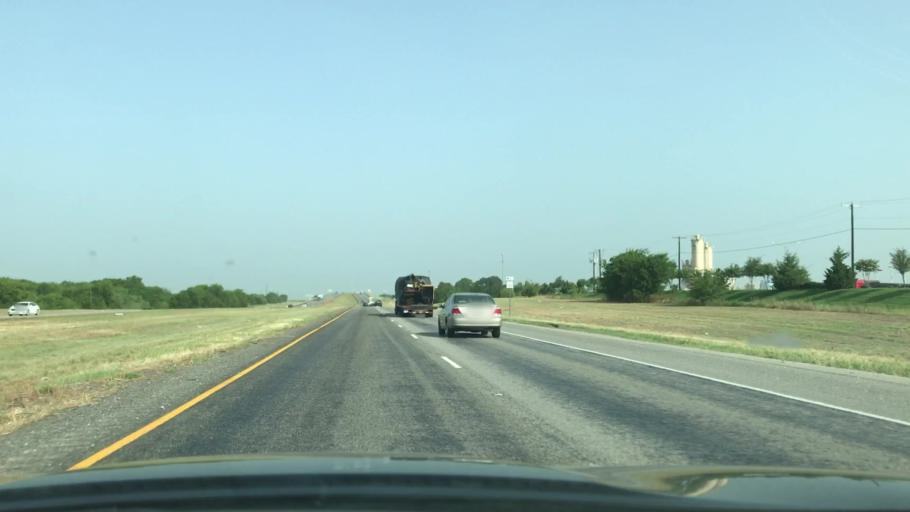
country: US
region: Texas
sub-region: Kaufman County
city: Talty
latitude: 32.7336
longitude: -96.3467
